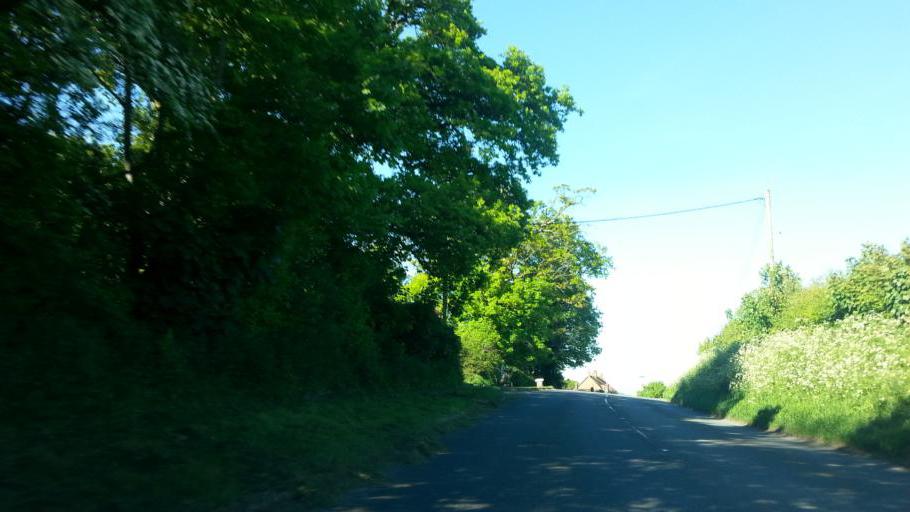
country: GB
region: England
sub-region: Dorset
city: Stalbridge
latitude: 50.9732
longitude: -2.4176
